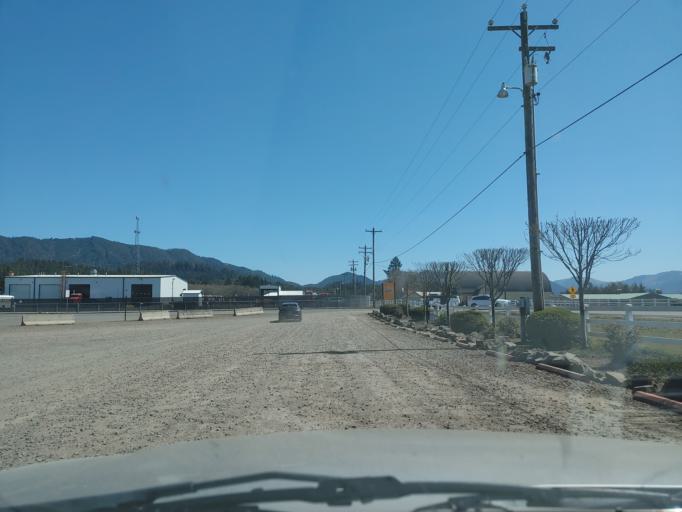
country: US
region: Oregon
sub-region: Tillamook County
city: Tillamook
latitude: 45.4821
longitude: -123.8440
